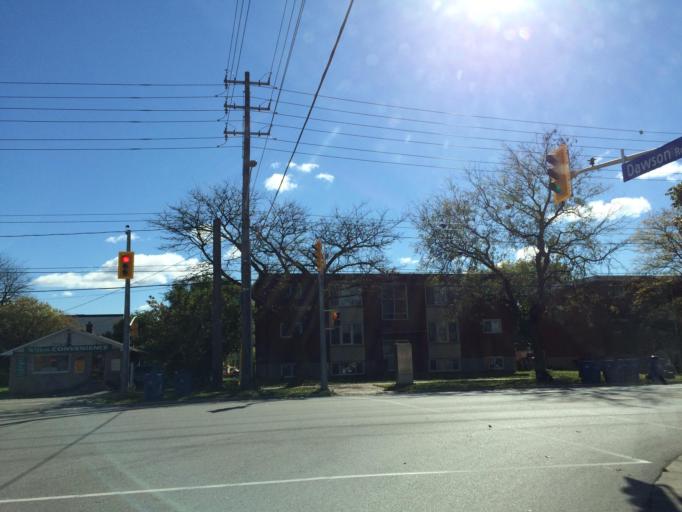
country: CA
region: Ontario
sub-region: Wellington County
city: Guelph
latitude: 43.5446
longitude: -80.2727
